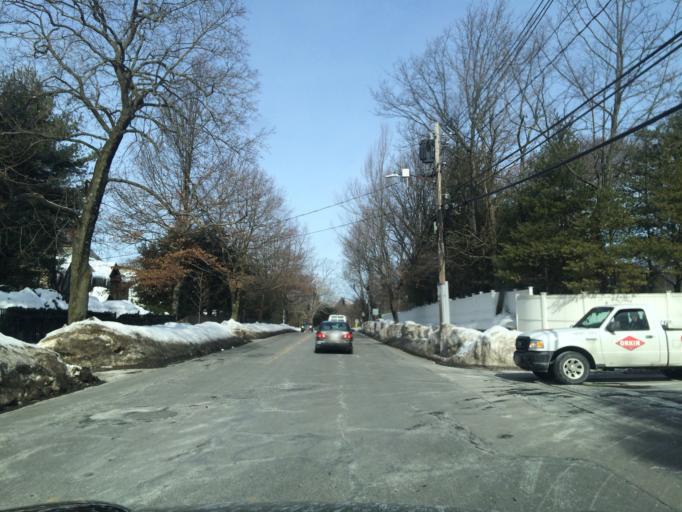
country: US
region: Massachusetts
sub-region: Norfolk County
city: Brookline
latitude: 42.3320
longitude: -71.1465
